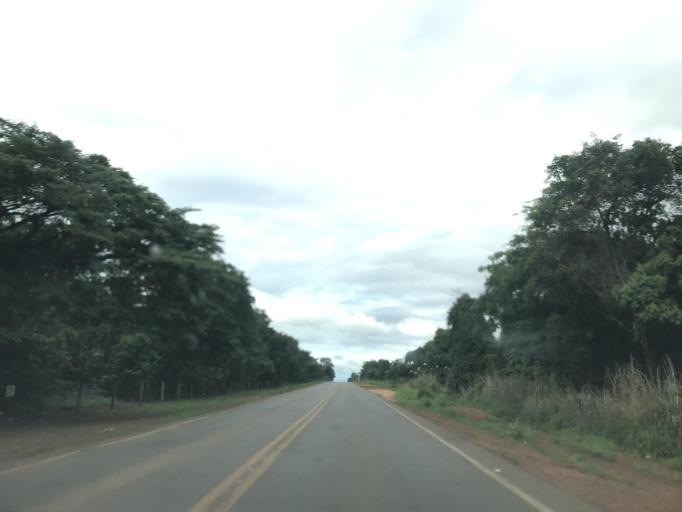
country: BR
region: Goias
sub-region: Vianopolis
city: Vianopolis
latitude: -16.7246
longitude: -48.4127
